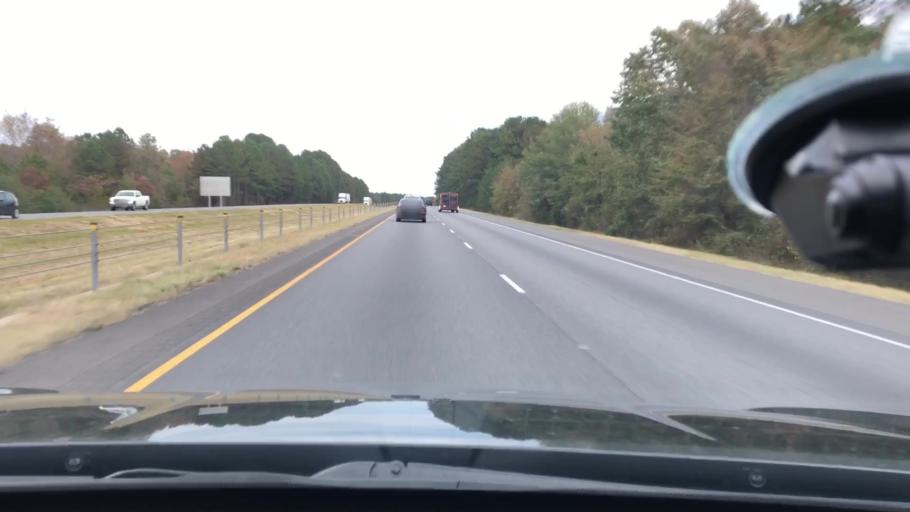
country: US
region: Arkansas
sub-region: Clark County
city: Arkadelphia
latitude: 34.2002
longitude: -93.0507
